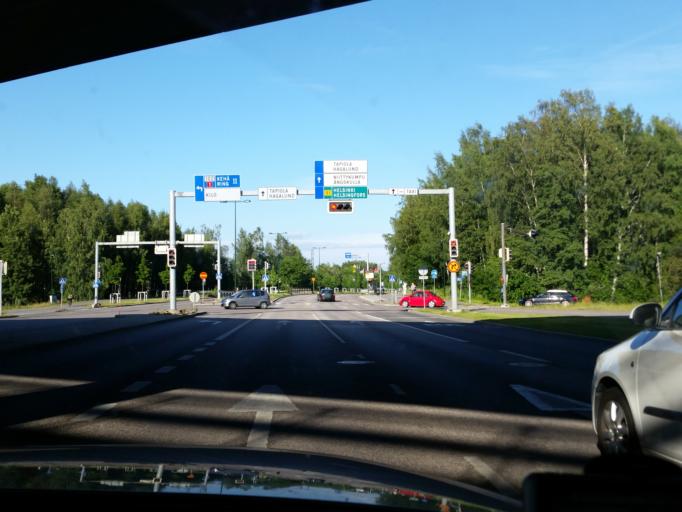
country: FI
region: Uusimaa
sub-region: Helsinki
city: Koukkuniemi
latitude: 60.1701
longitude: 24.7534
